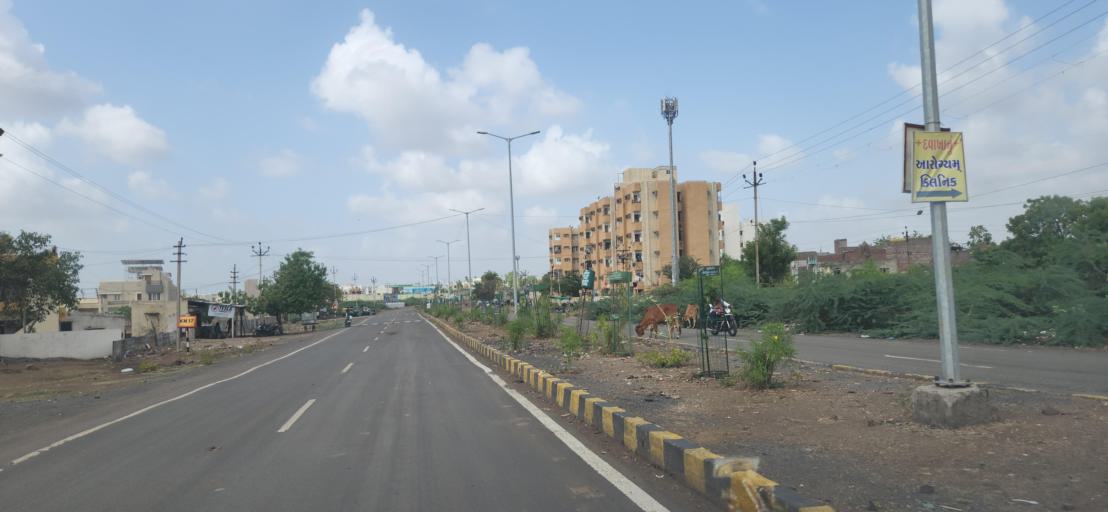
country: IN
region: Gujarat
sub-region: Bhavnagar
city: Bhavnagar
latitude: 21.7585
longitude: 72.1739
